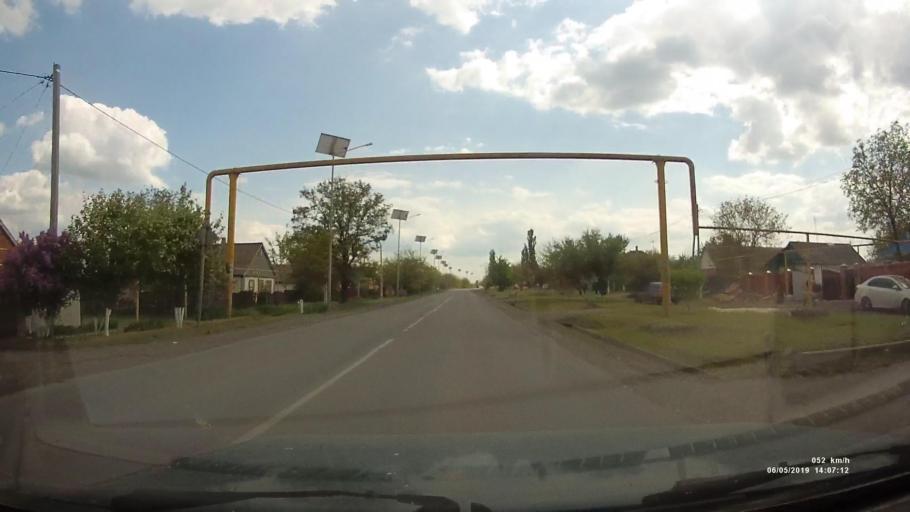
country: RU
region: Rostov
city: Shakhty
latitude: 47.6828
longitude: 40.3031
